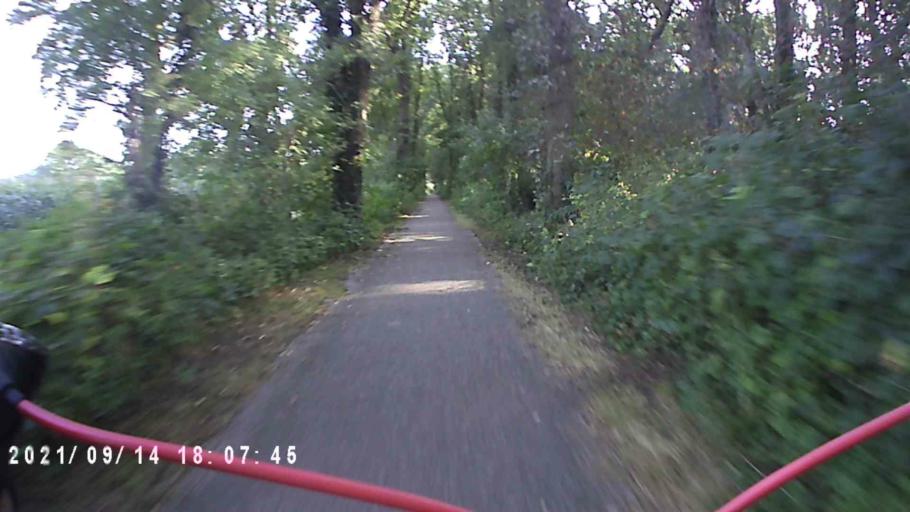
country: NL
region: Drenthe
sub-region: Gemeente Tynaarlo
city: Zuidlaren
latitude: 53.1031
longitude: 6.6567
